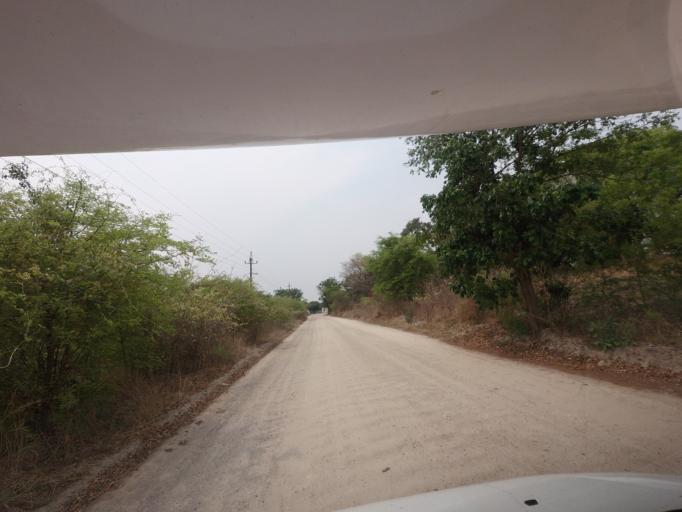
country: ZM
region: Western
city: Sesheke
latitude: -17.4880
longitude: 24.2855
